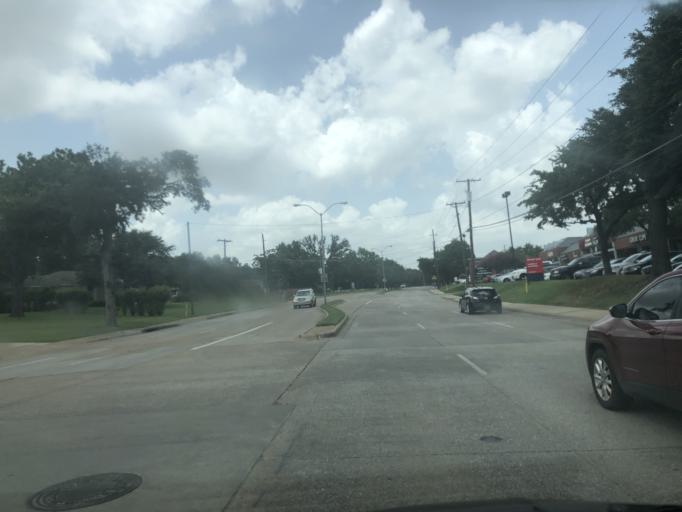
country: US
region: Texas
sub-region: Dallas County
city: University Park
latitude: 32.8647
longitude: -96.8368
